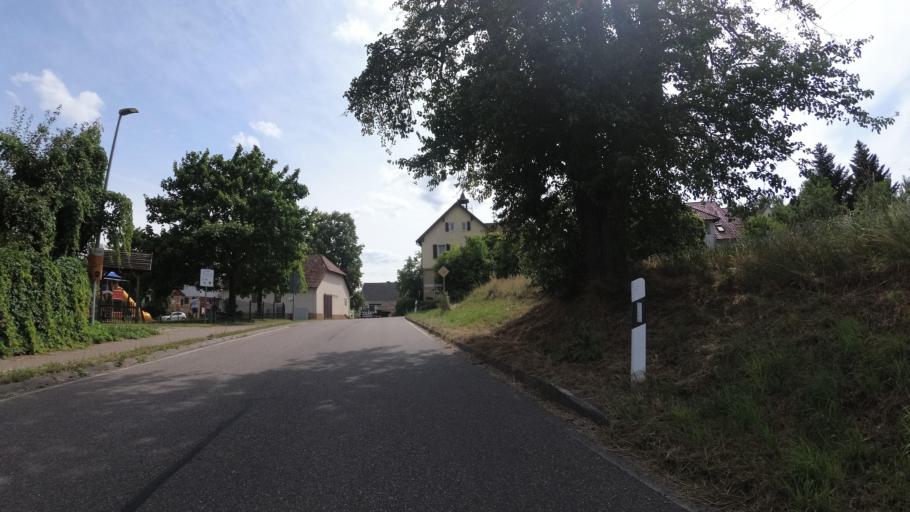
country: DE
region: Baden-Wuerttemberg
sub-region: Regierungsbezirk Stuttgart
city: Eberstadt
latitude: 49.1897
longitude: 9.3101
